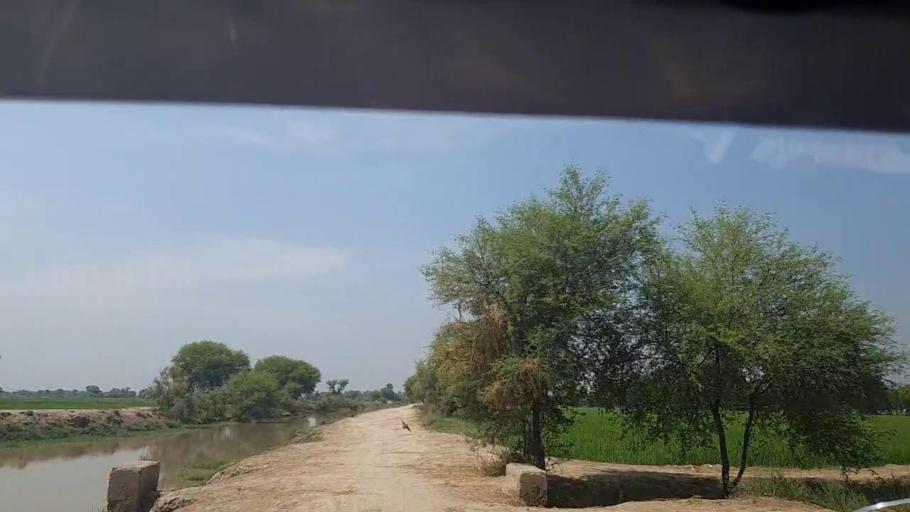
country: PK
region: Sindh
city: Thul
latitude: 28.1996
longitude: 68.7018
